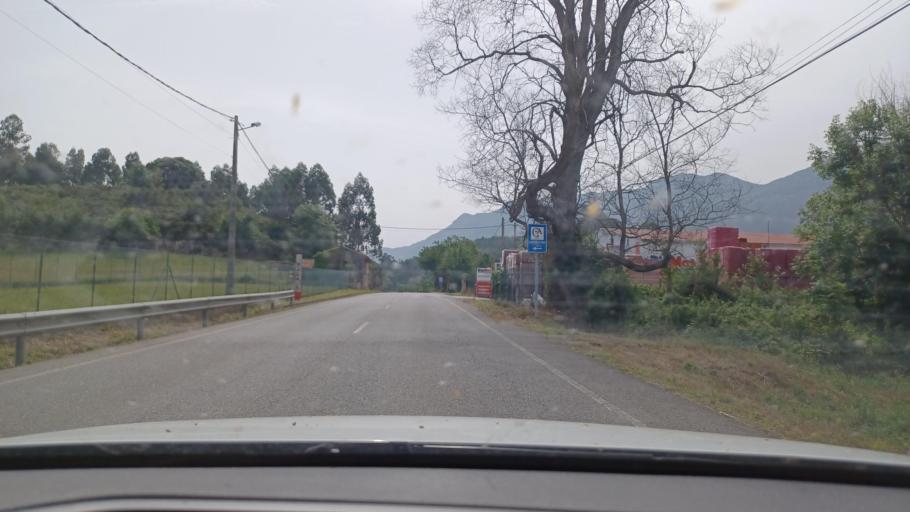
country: ES
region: Asturias
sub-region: Province of Asturias
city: Ribadesella
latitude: 43.4476
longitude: -5.0173
